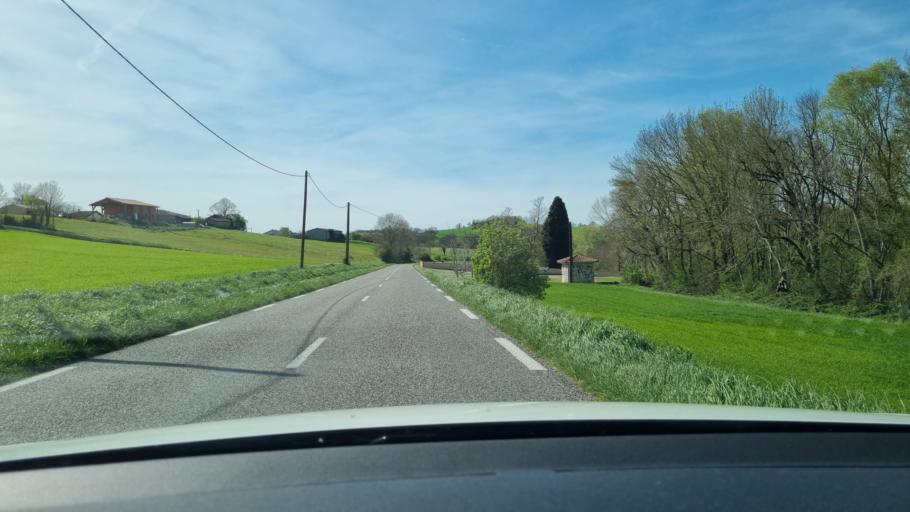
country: FR
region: Midi-Pyrenees
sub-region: Departement du Gers
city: Samatan
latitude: 43.4909
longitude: 1.0073
